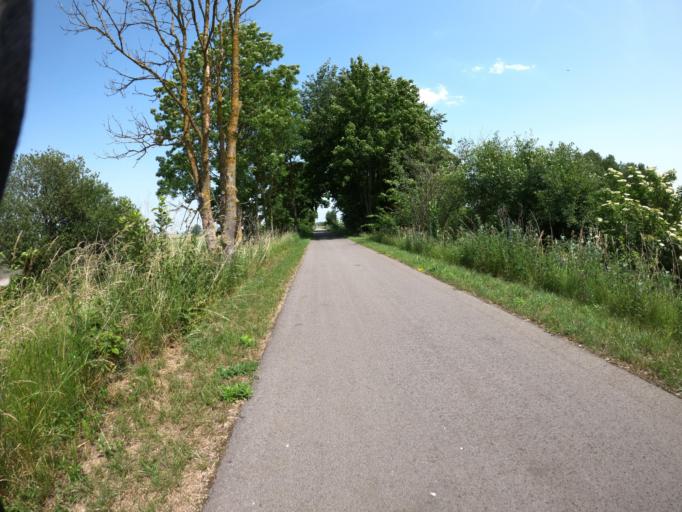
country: PL
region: West Pomeranian Voivodeship
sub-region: Powiat choszczenski
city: Pelczyce
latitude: 53.1170
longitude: 15.3482
